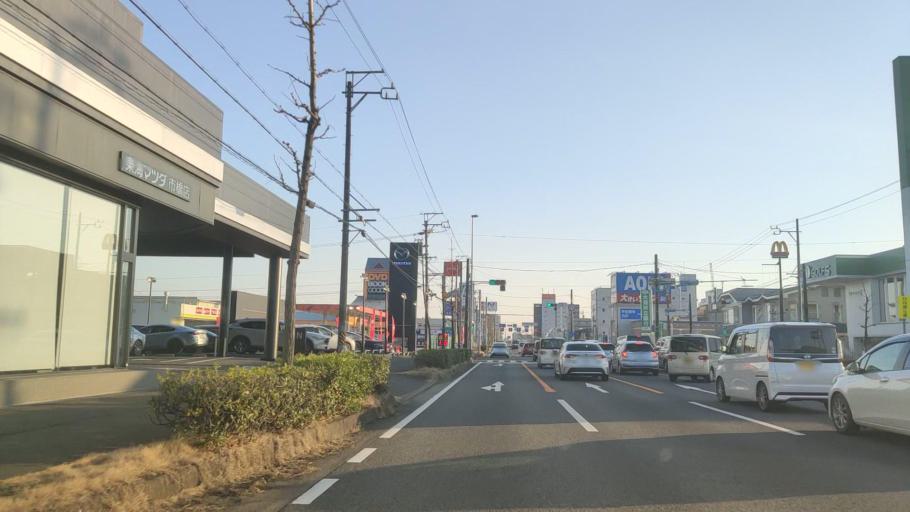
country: JP
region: Gifu
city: Gifu-shi
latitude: 35.3988
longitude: 136.7266
